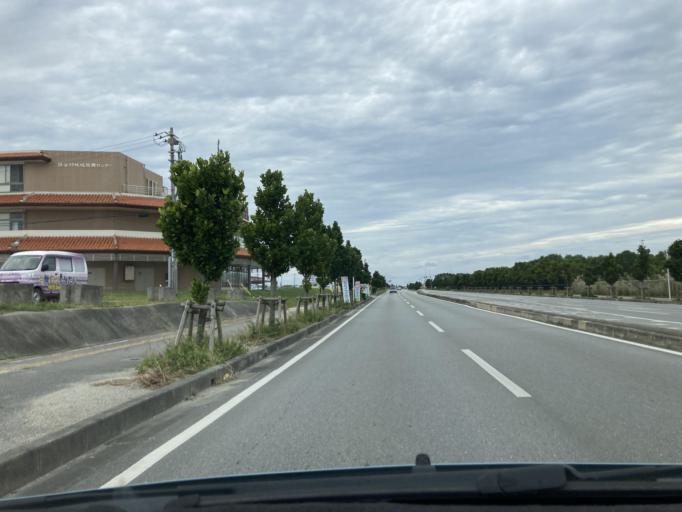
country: JP
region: Okinawa
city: Okinawa
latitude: 26.3934
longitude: 127.7468
